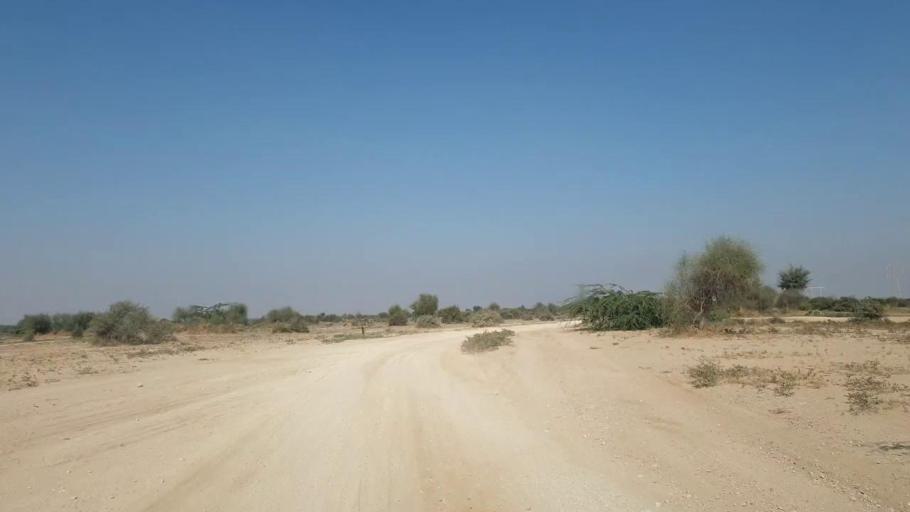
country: PK
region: Sindh
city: Jamshoro
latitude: 25.2935
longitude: 67.8137
